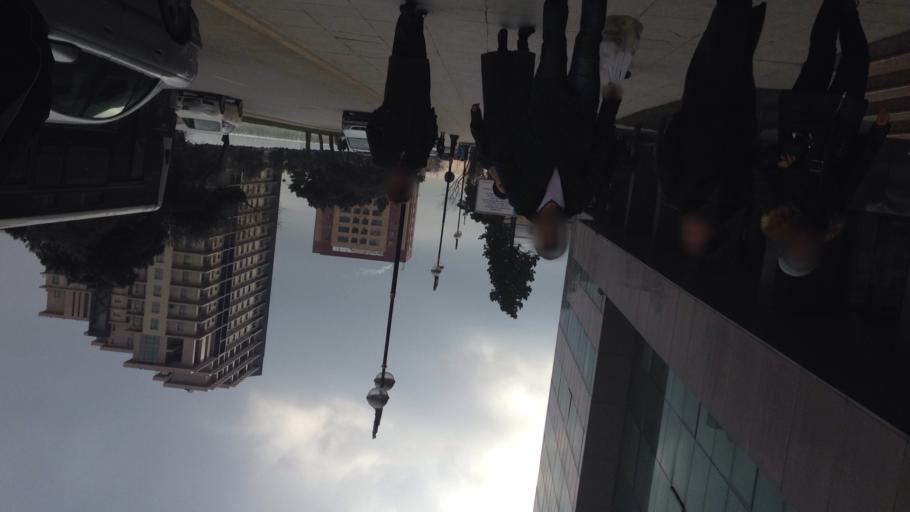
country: AZ
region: Baki
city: Baku
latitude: 40.3803
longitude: 49.8649
